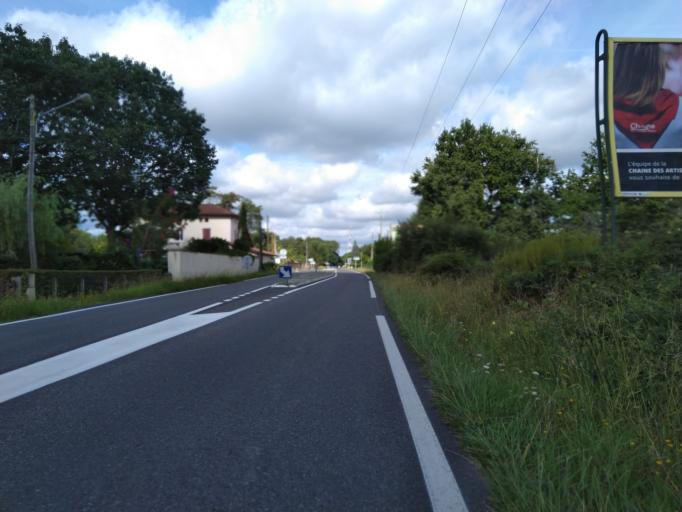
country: FR
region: Aquitaine
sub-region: Departement des Landes
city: Mees
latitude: 43.7316
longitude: -1.0986
